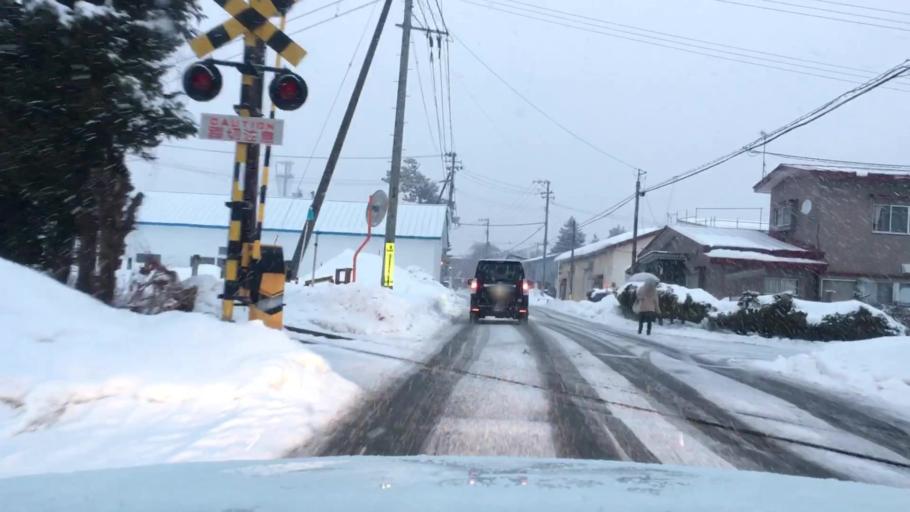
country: JP
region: Aomori
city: Hirosaki
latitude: 40.5645
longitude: 140.4858
